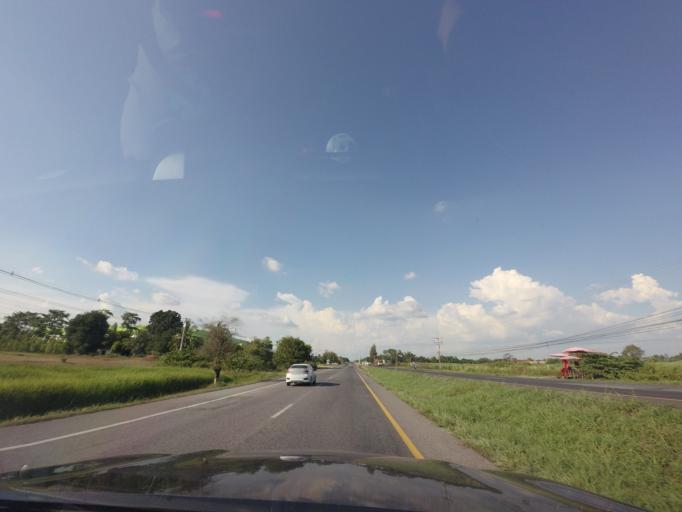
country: TH
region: Khon Kaen
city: Non Sila
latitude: 16.0031
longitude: 102.7026
